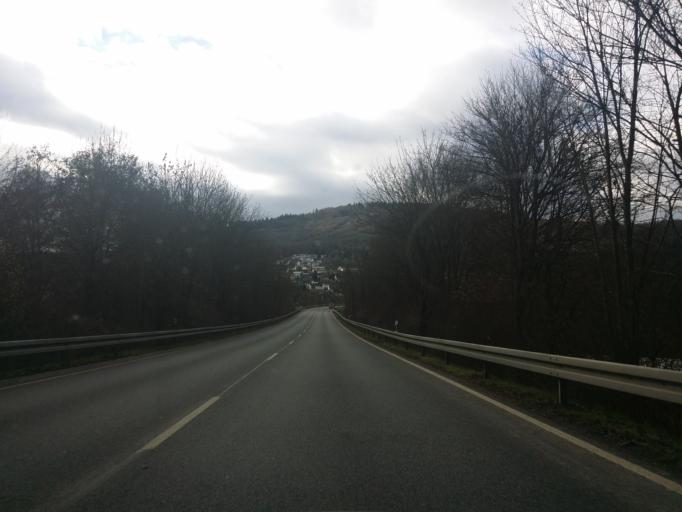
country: DE
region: Hesse
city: Kelkheim (Taunus)
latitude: 50.1541
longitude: 8.4257
